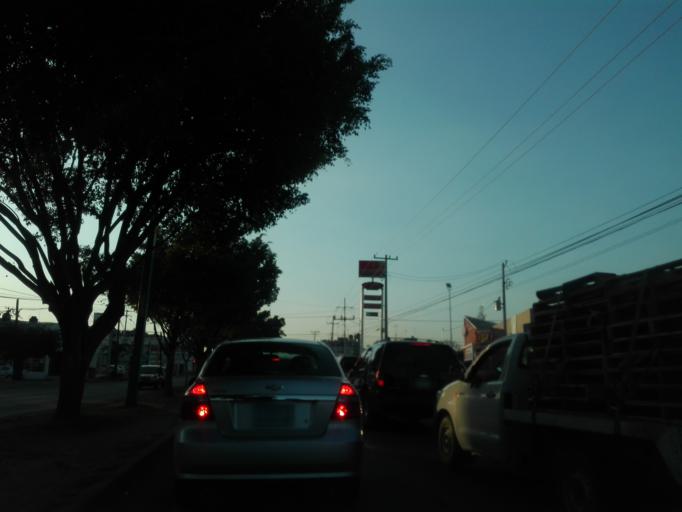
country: MX
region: Guanajuato
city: Leon
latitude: 21.1283
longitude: -101.6456
